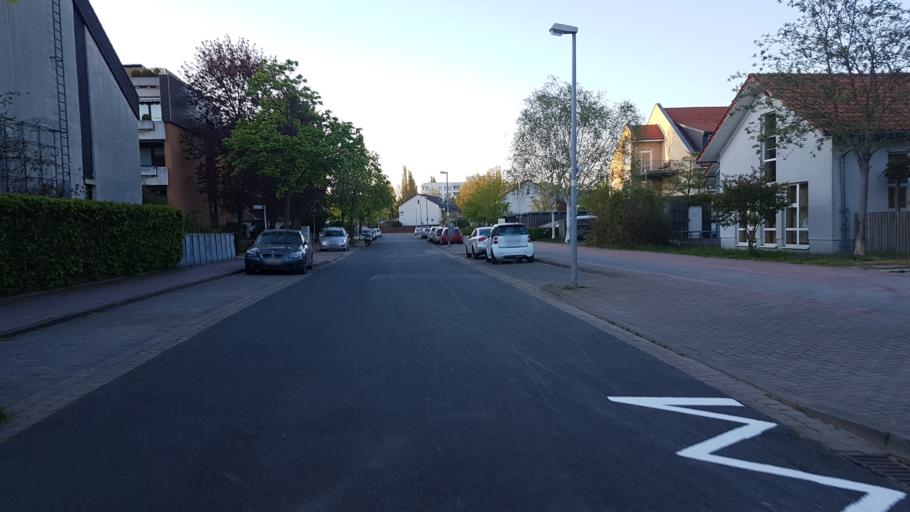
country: DE
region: Lower Saxony
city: Langenhagen
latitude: 52.4162
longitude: 9.7662
